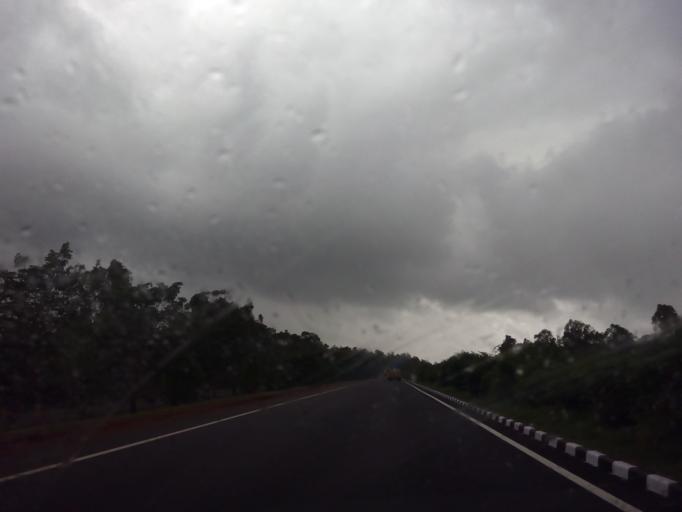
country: IN
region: Karnataka
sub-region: Belgaum
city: Belgaum
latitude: 16.0145
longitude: 74.5176
